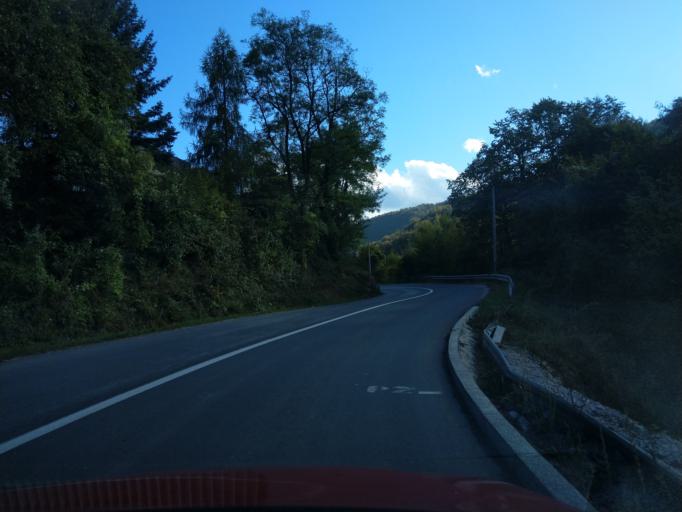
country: RS
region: Central Serbia
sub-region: Zlatiborski Okrug
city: Uzice
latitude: 43.8762
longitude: 19.7919
